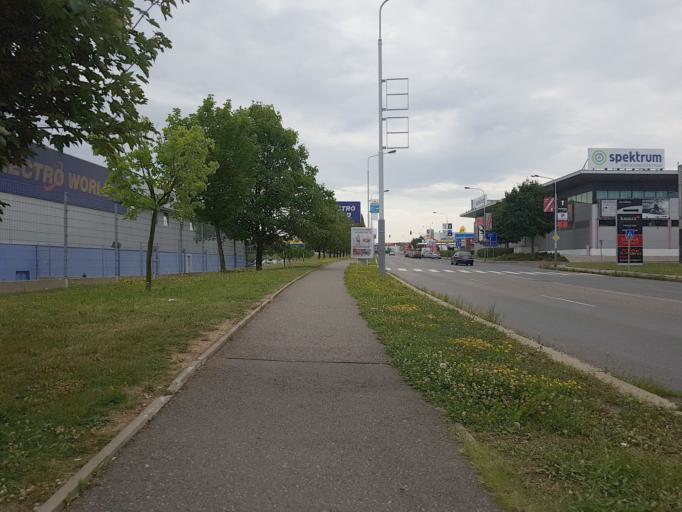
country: CZ
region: Central Bohemia
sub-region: Okres Praha-Zapad
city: Pruhonice
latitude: 50.0062
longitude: 14.5721
